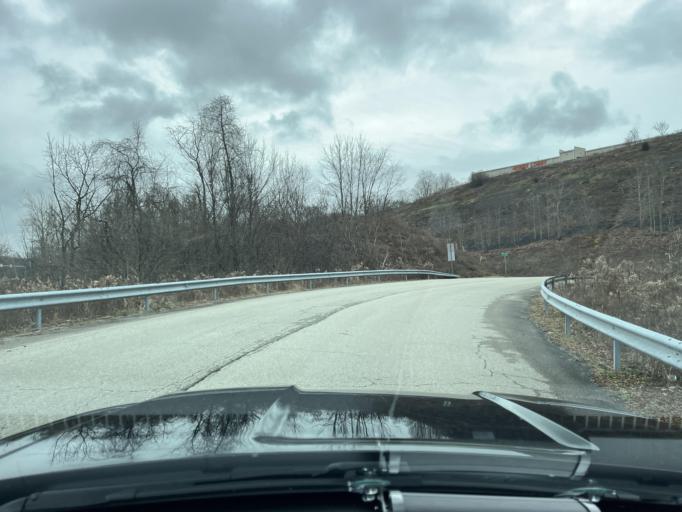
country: US
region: Pennsylvania
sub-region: Fayette County
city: South Uniontown
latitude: 39.9187
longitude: -79.7564
